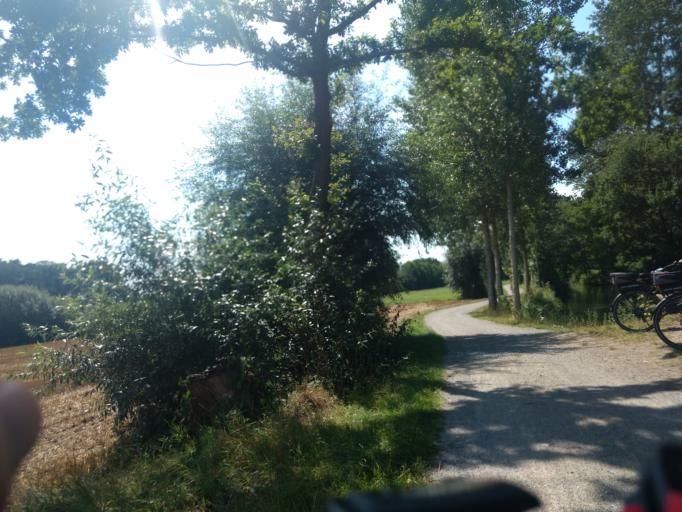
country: DE
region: North Rhine-Westphalia
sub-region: Regierungsbezirk Detmold
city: Delbruck
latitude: 51.7650
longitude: 8.6178
